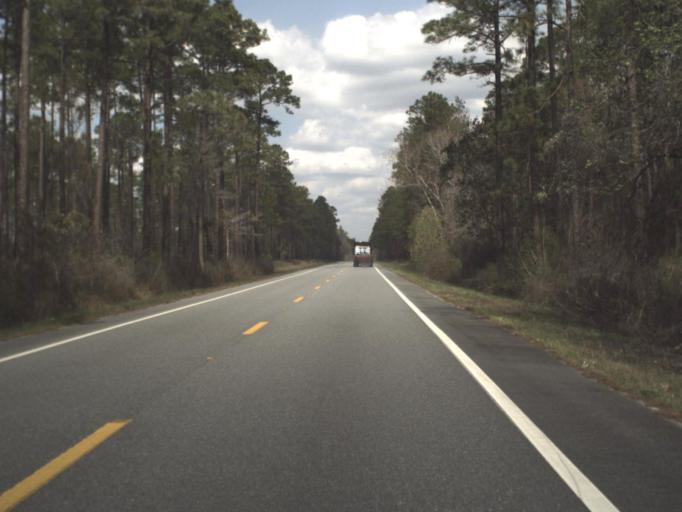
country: US
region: Florida
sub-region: Franklin County
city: Apalachicola
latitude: 29.9096
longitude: -84.9776
